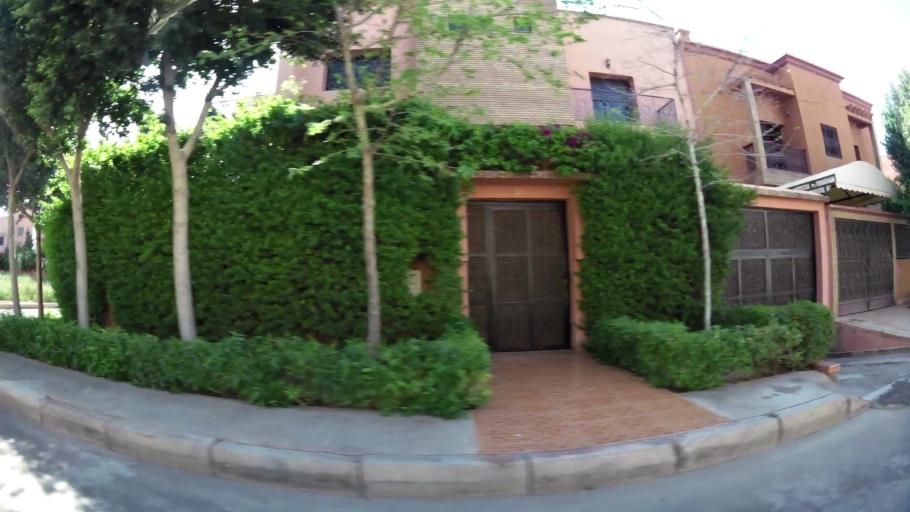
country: MA
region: Marrakech-Tensift-Al Haouz
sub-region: Marrakech
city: Marrakesh
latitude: 31.6459
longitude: -8.0425
